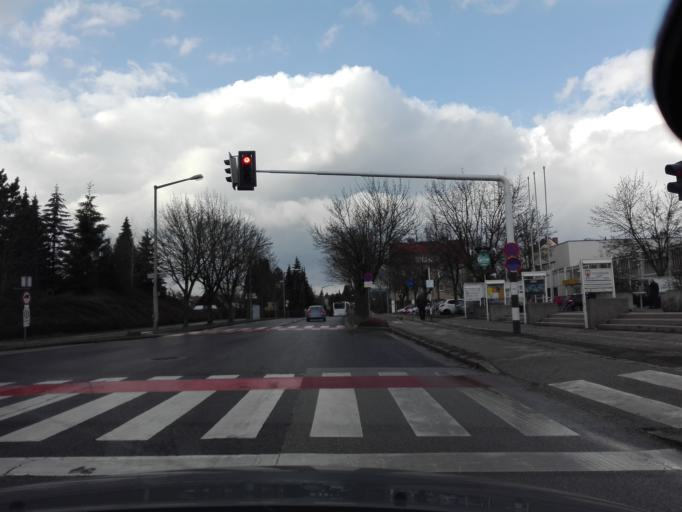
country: AT
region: Upper Austria
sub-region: Politischer Bezirk Linz-Land
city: Leonding
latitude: 48.2705
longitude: 14.2825
